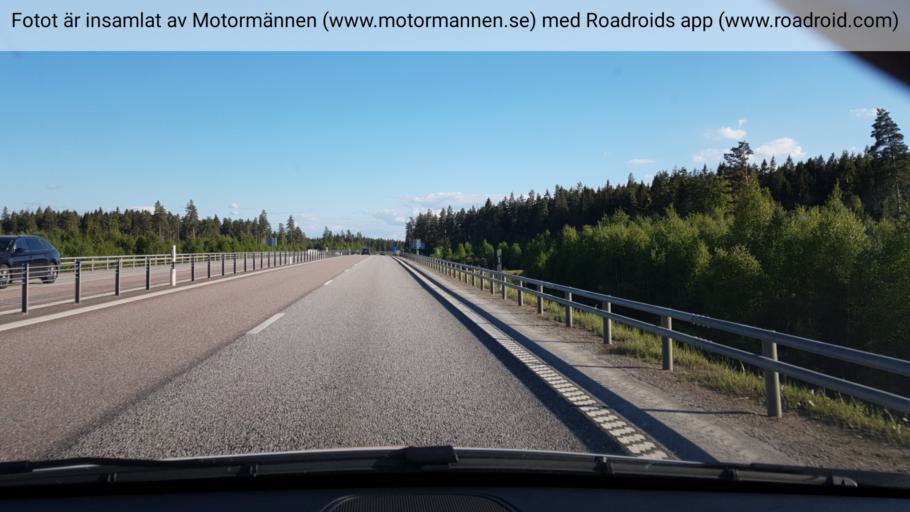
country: SE
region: Vaestra Goetaland
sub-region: Skovde Kommun
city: Skultorp
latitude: 58.3489
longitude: 13.8652
